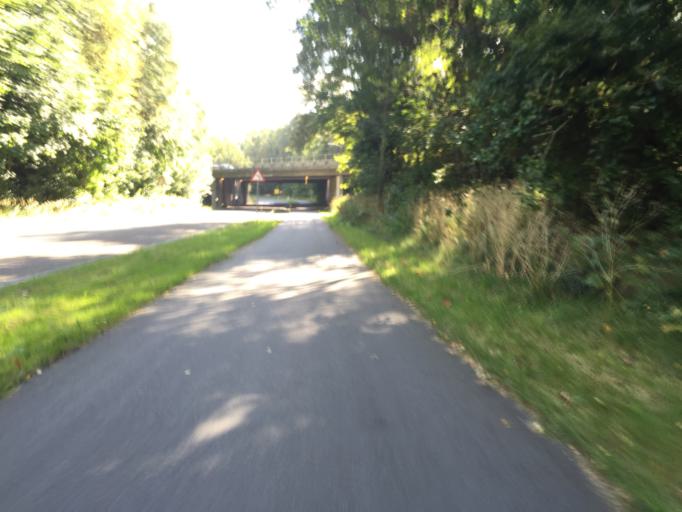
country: DK
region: Capital Region
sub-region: Herlev Kommune
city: Herlev
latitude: 55.7685
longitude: 12.4287
